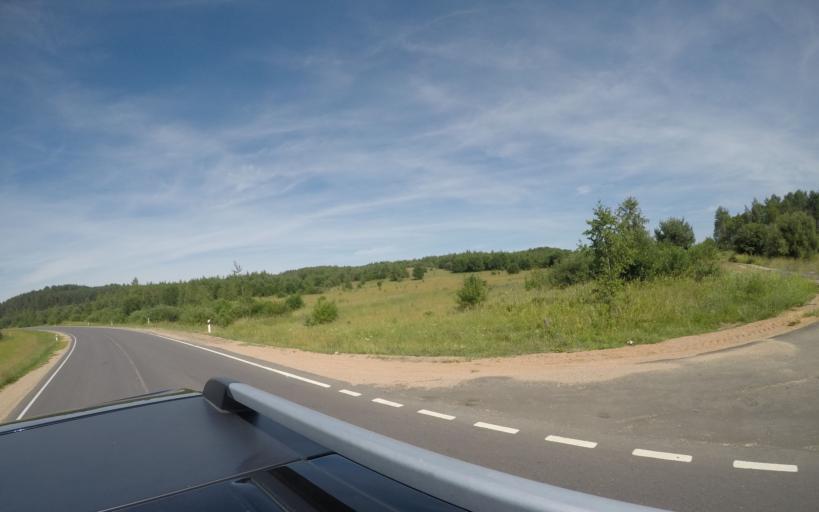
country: BY
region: Grodnenskaya
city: Hal'shany
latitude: 54.2670
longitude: 26.0294
